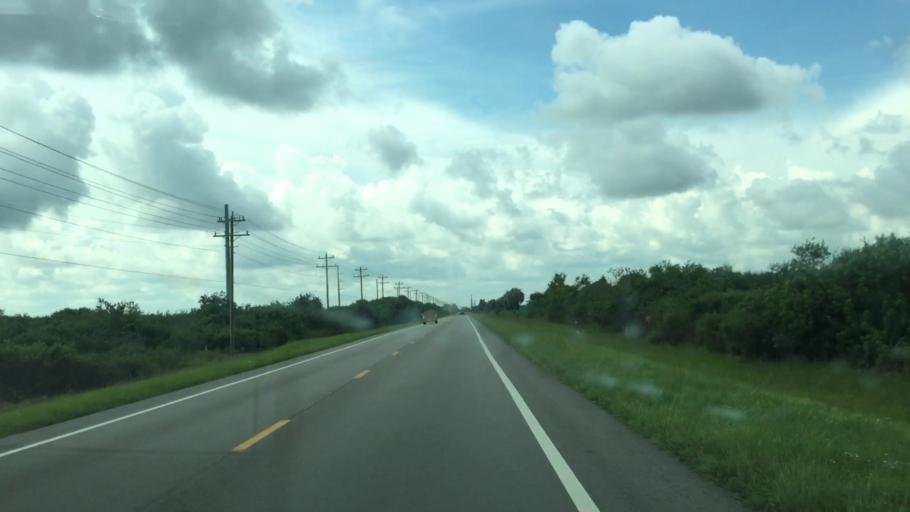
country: US
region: Florida
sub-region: Collier County
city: Immokalee
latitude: 26.3848
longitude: -81.4171
